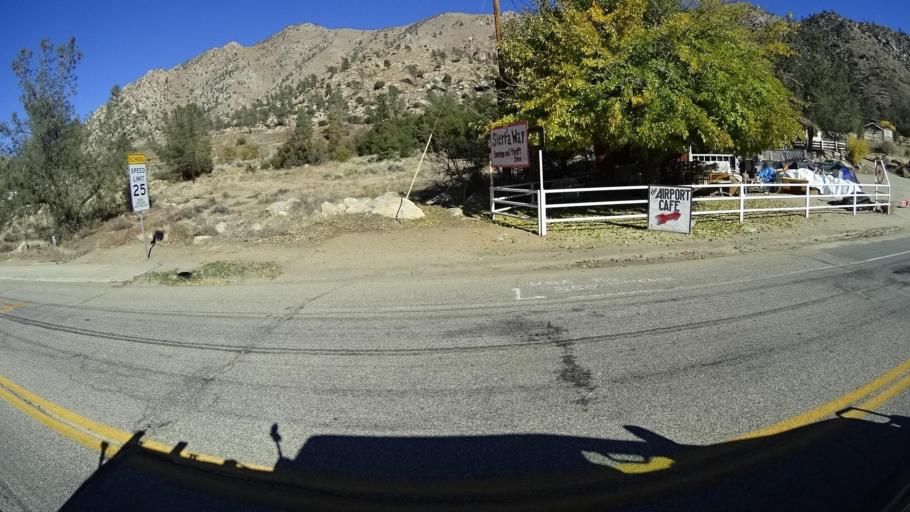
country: US
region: California
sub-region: Kern County
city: Kernville
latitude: 35.7553
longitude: -118.4192
